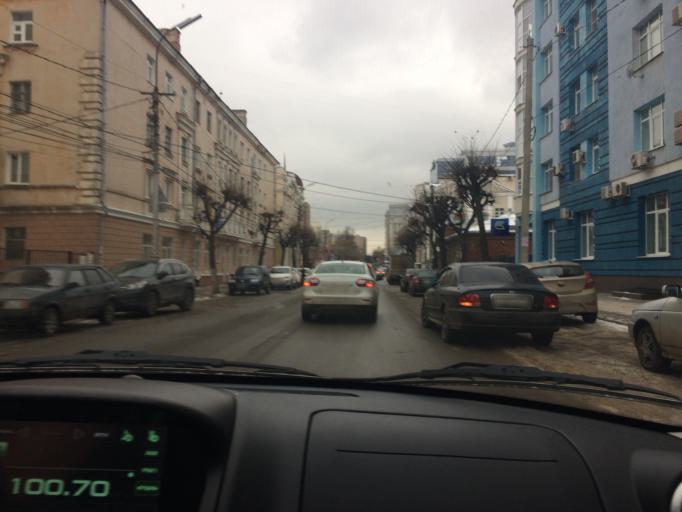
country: RU
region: Rjazan
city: Ryazan'
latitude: 54.6249
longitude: 39.7541
